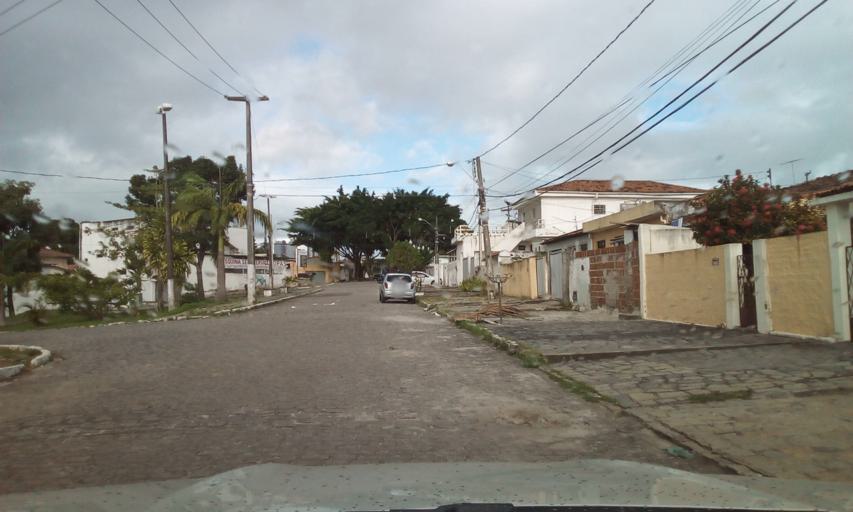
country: BR
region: Paraiba
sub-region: Joao Pessoa
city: Joao Pessoa
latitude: -7.1296
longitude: -34.8453
